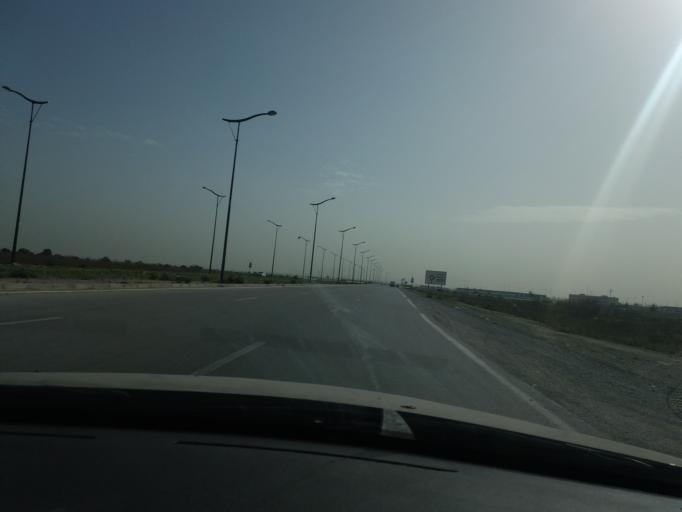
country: TN
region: Tunis
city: Tunis
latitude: 36.8067
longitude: 10.1936
